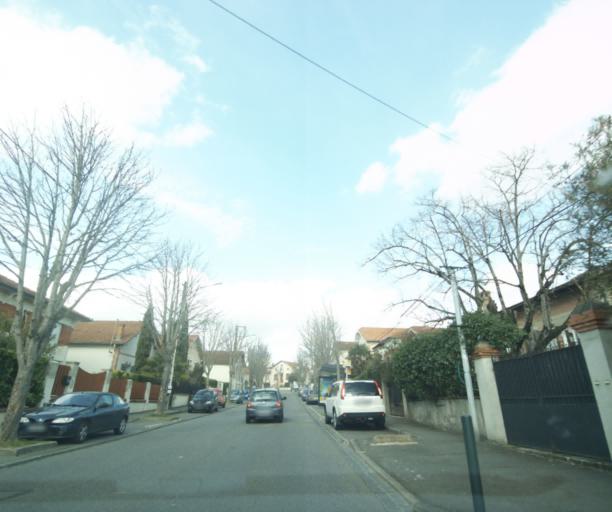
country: FR
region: Midi-Pyrenees
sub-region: Departement de la Haute-Garonne
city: Toulouse
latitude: 43.5942
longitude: 1.4731
